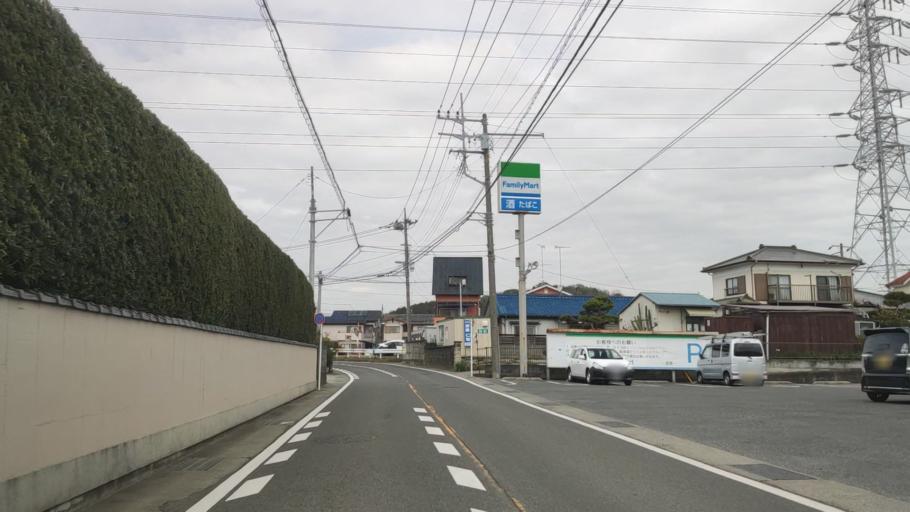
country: JP
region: Kanagawa
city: Ninomiya
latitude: 35.2973
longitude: 139.2326
